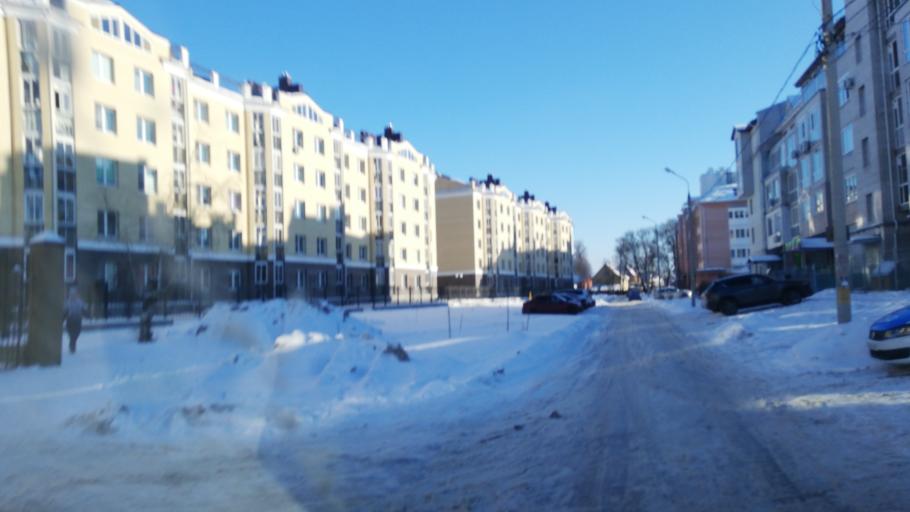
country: RU
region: Jaroslavl
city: Yaroslavl
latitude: 57.6110
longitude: 39.8976
